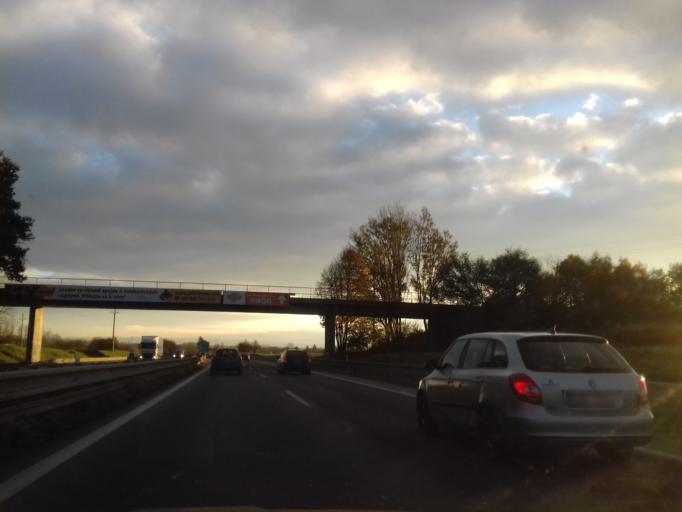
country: CZ
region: Olomoucky
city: Vrbatky
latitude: 49.5293
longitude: 17.1665
